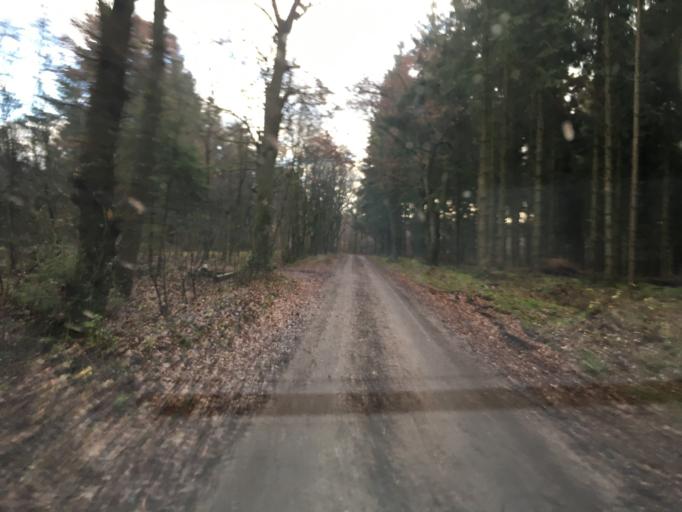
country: DK
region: South Denmark
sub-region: Tonder Kommune
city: Logumkloster
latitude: 55.1276
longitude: 8.8800
